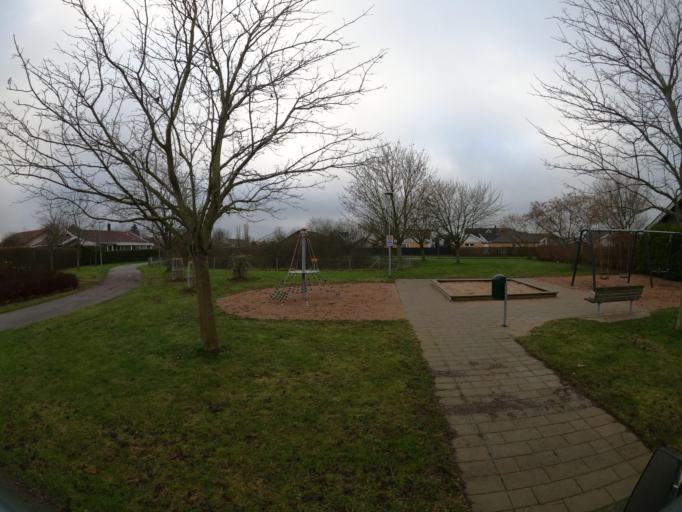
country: SE
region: Skane
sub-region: Svedala Kommun
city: Svedala
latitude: 55.5227
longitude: 13.2244
